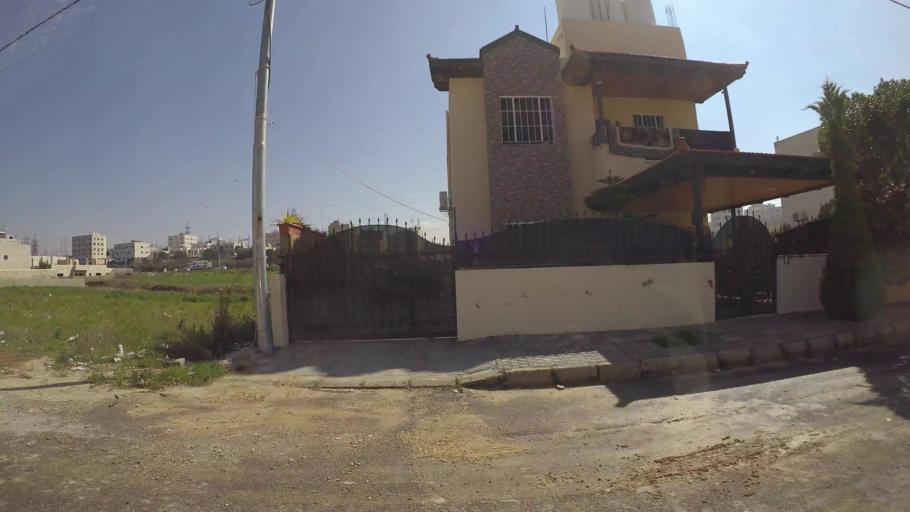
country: JO
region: Amman
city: Al Bunayyat ash Shamaliyah
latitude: 31.8903
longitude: 35.9014
